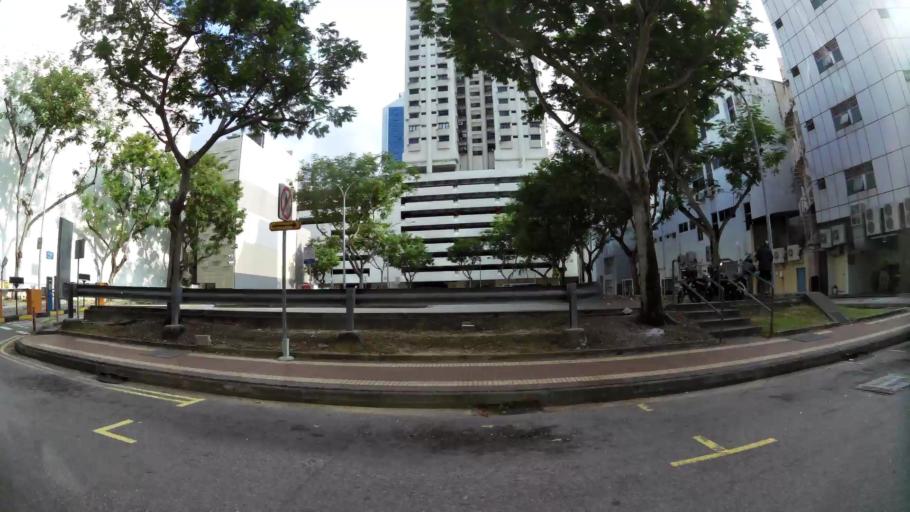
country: SG
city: Singapore
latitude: 1.2880
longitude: 103.8481
